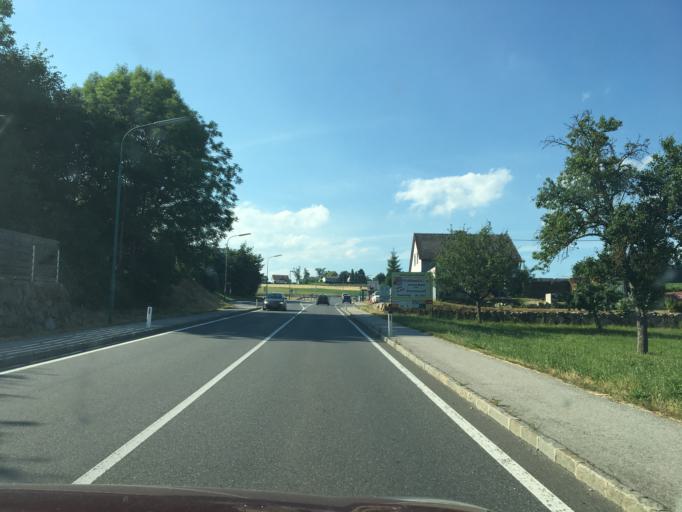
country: AT
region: Lower Austria
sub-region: Politischer Bezirk Amstetten
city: Ennsdorf
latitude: 48.2681
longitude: 14.5466
